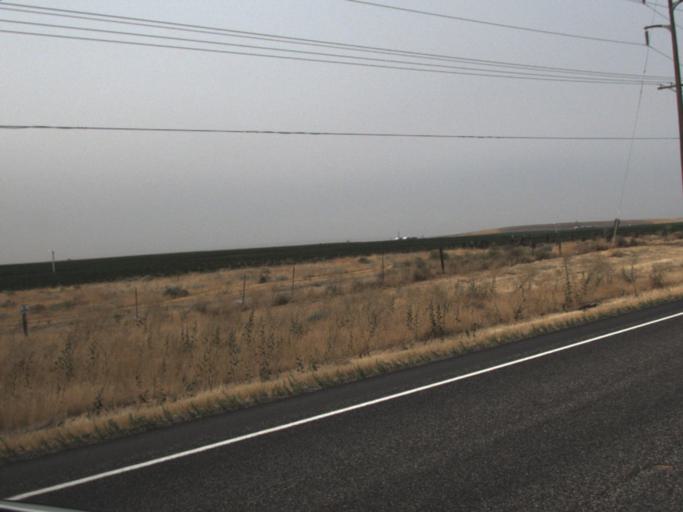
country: US
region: Oregon
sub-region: Morrow County
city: Irrigon
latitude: 45.9907
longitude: -119.6029
